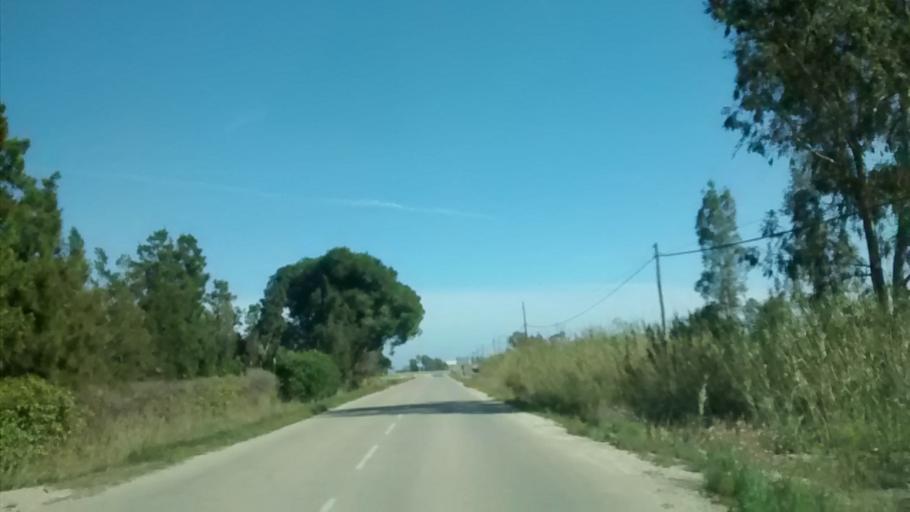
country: ES
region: Catalonia
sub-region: Provincia de Tarragona
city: Deltebre
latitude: 40.7126
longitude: 0.7536
